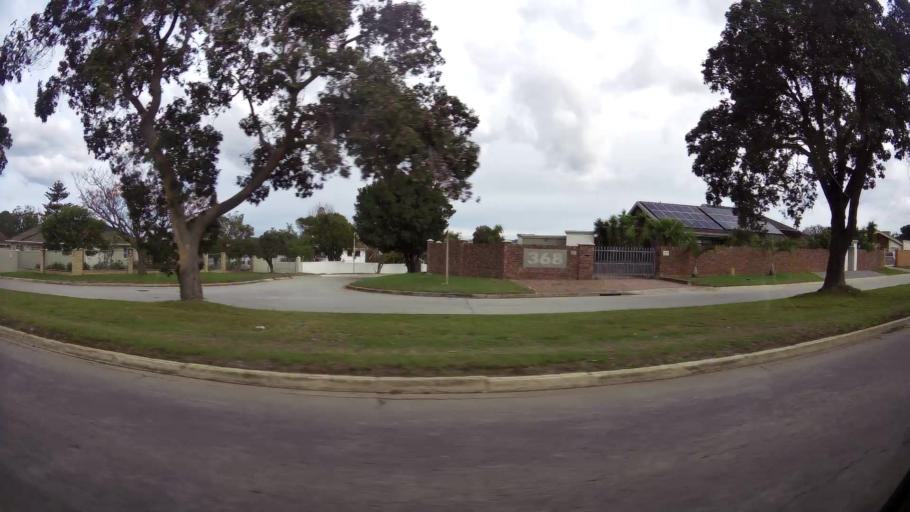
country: ZA
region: Eastern Cape
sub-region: Nelson Mandela Bay Metropolitan Municipality
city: Port Elizabeth
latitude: -33.9467
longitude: 25.5505
